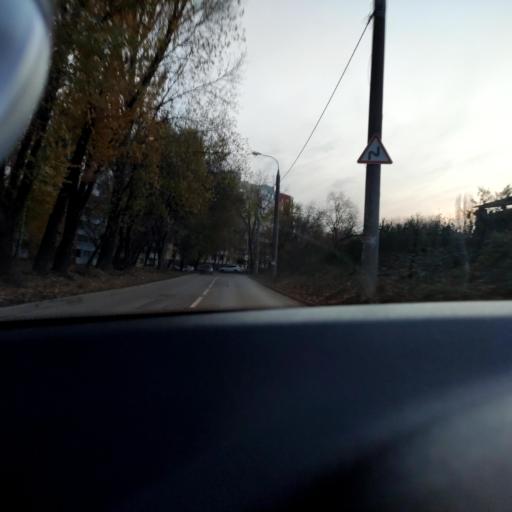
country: RU
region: Samara
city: Samara
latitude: 53.2456
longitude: 50.2161
